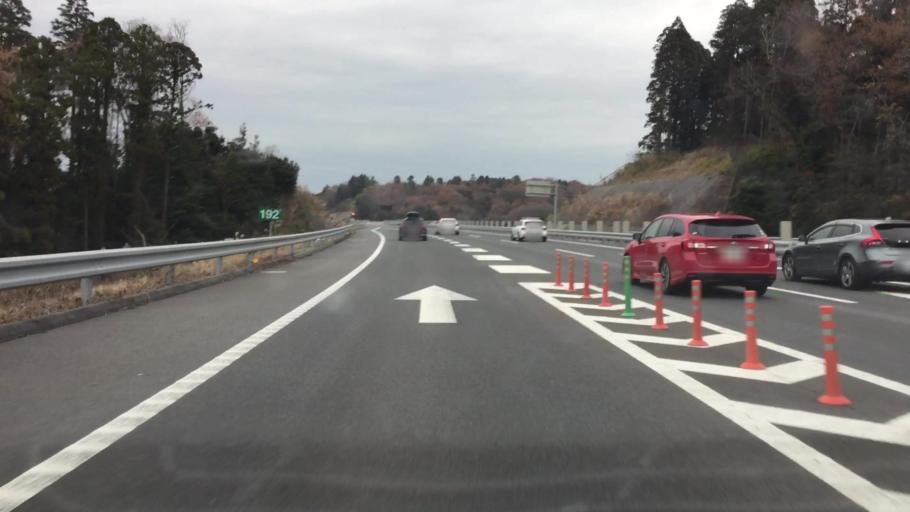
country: JP
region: Chiba
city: Sawara
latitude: 35.8643
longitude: 140.3916
